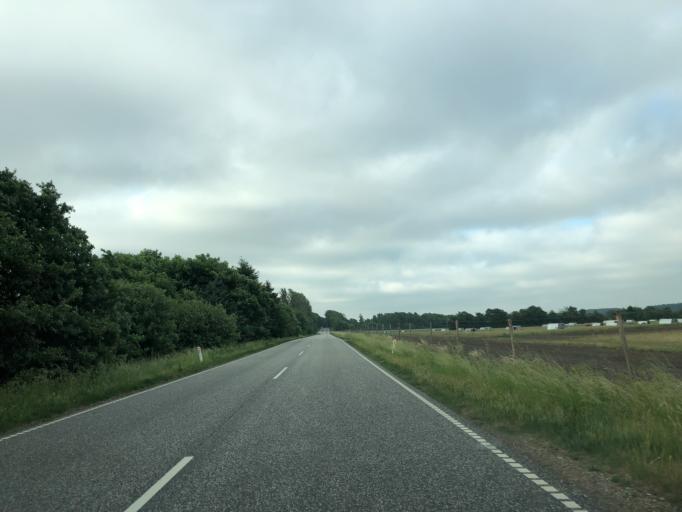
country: DK
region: South Denmark
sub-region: Vejle Kommune
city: Give
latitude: 55.8723
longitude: 9.2360
